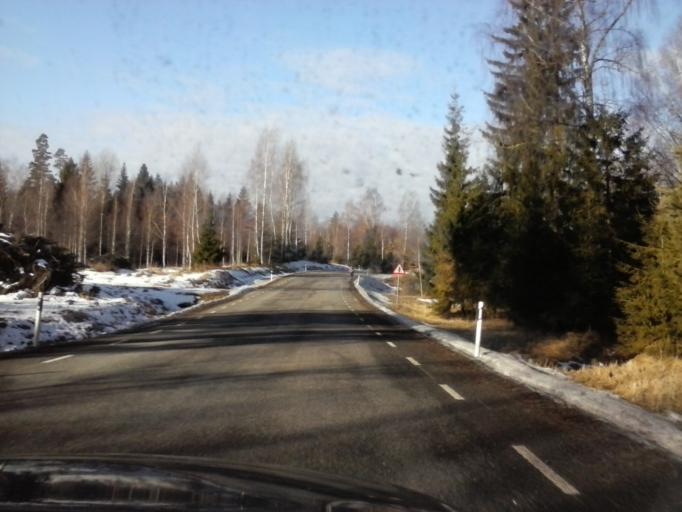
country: EE
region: Tartu
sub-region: Elva linn
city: Elva
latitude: 58.0483
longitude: 26.4280
